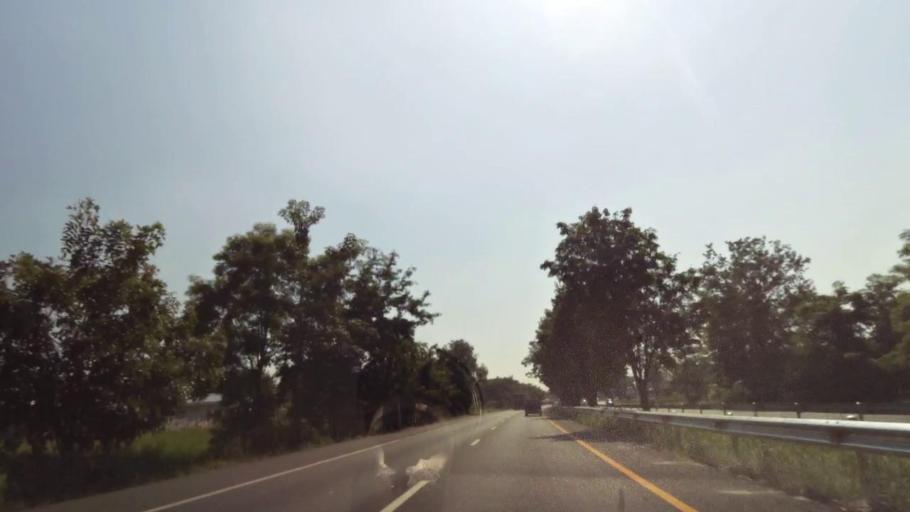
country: TH
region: Nakhon Sawan
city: Kao Liao
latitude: 15.9642
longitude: 100.1197
